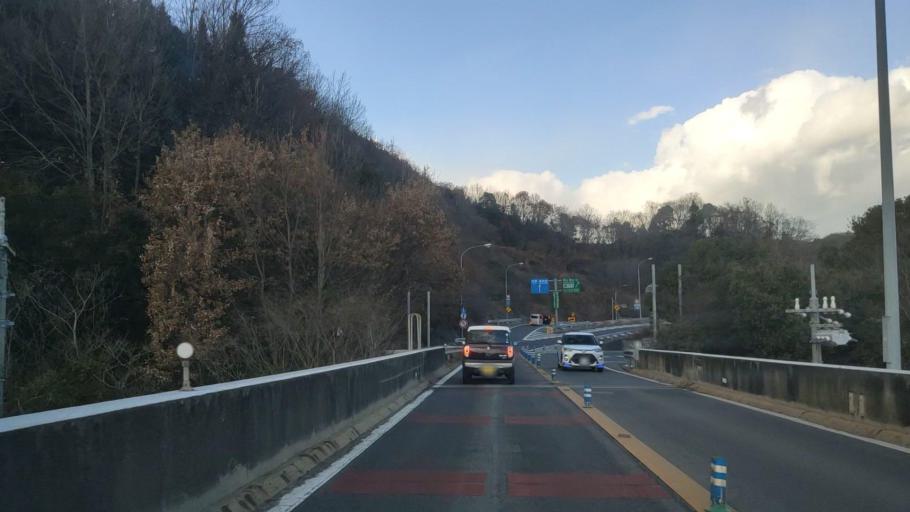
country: JP
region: Hiroshima
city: Onomichi
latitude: 34.4322
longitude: 133.2175
